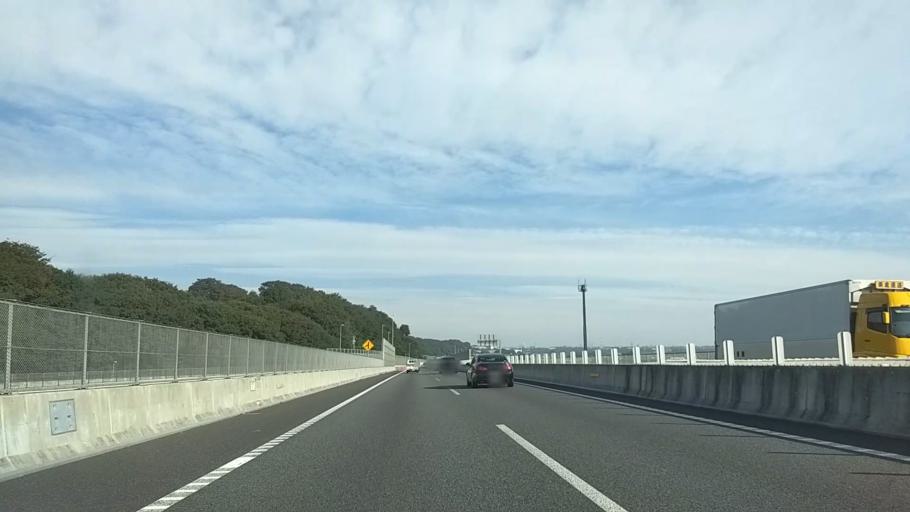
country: JP
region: Kanagawa
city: Zama
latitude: 35.4891
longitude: 139.3695
